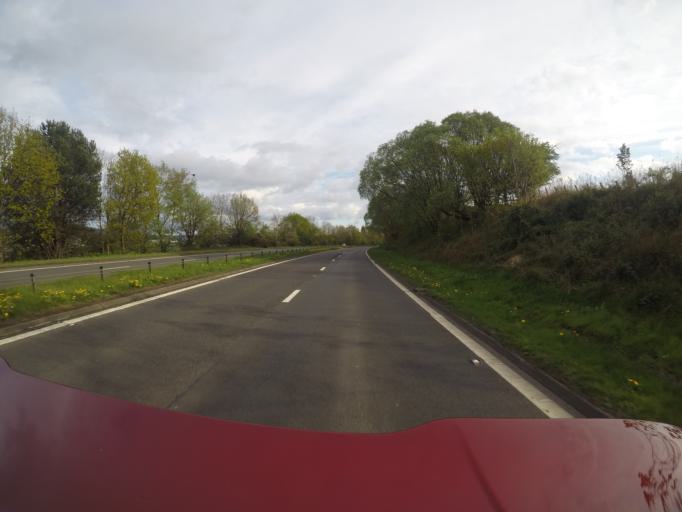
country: GB
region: Scotland
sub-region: West Dunbartonshire
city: Alexandria
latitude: 55.9845
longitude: -4.5873
